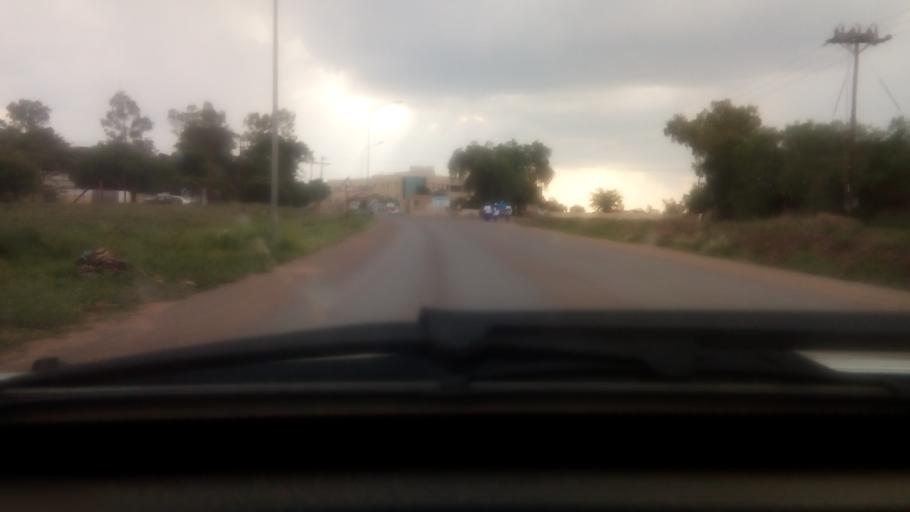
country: BW
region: Kweneng
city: Molepolole
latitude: -24.4112
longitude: 25.4897
